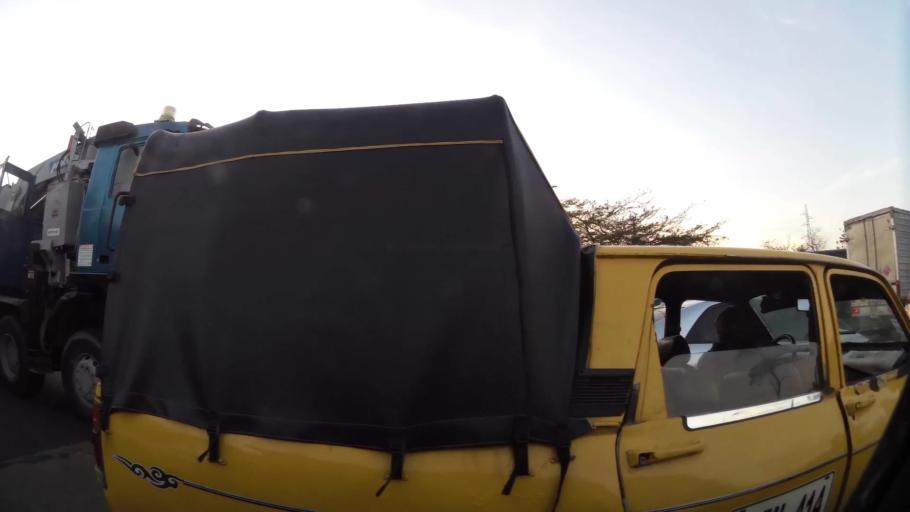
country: CO
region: Atlantico
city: Soledad
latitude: 10.9340
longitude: -74.7807
